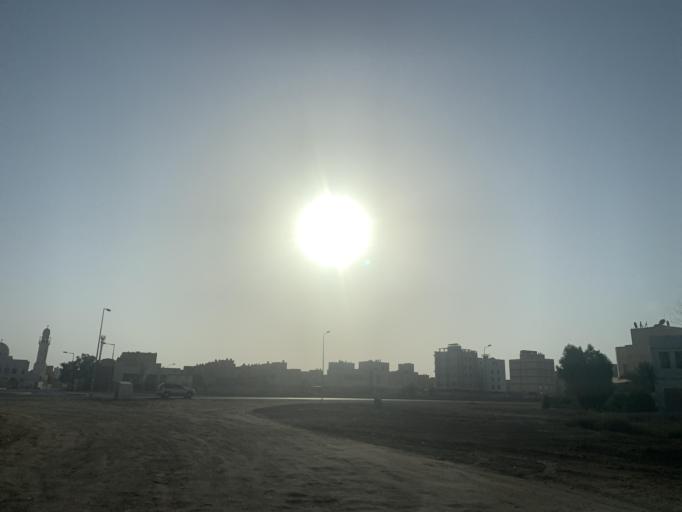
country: BH
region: Manama
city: Jidd Hafs
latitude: 26.2104
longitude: 50.5254
